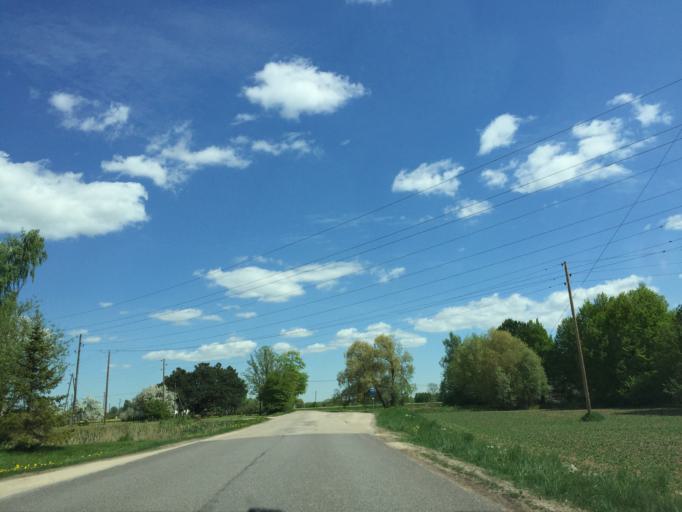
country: LV
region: Bauskas Rajons
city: Bauska
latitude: 56.4065
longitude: 24.1598
